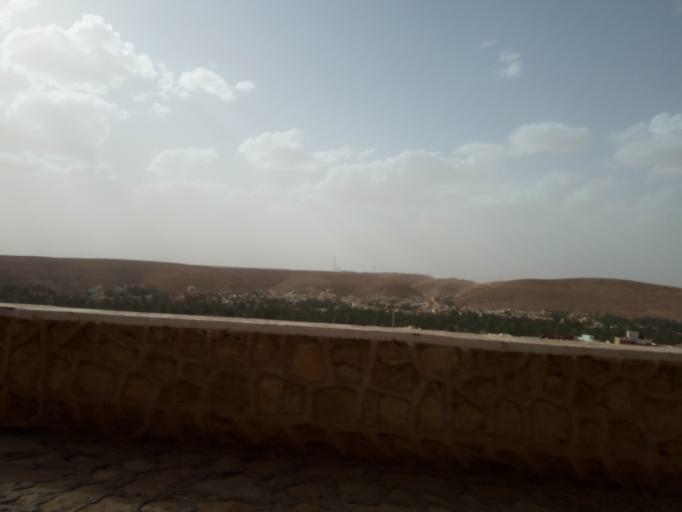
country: DZ
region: Ghardaia
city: Ghardaia
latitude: 32.4640
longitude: 3.6900
